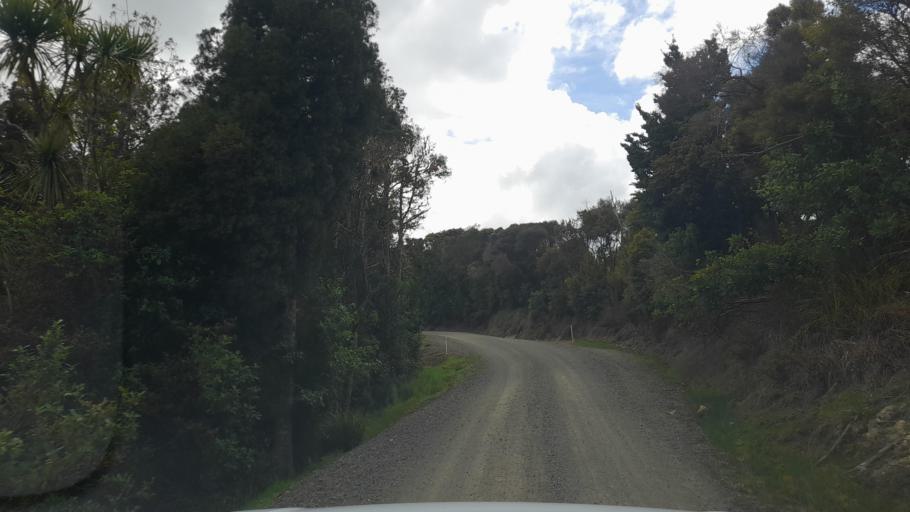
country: NZ
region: Auckland
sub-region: Auckland
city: Wellsford
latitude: -36.2065
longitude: 174.3357
